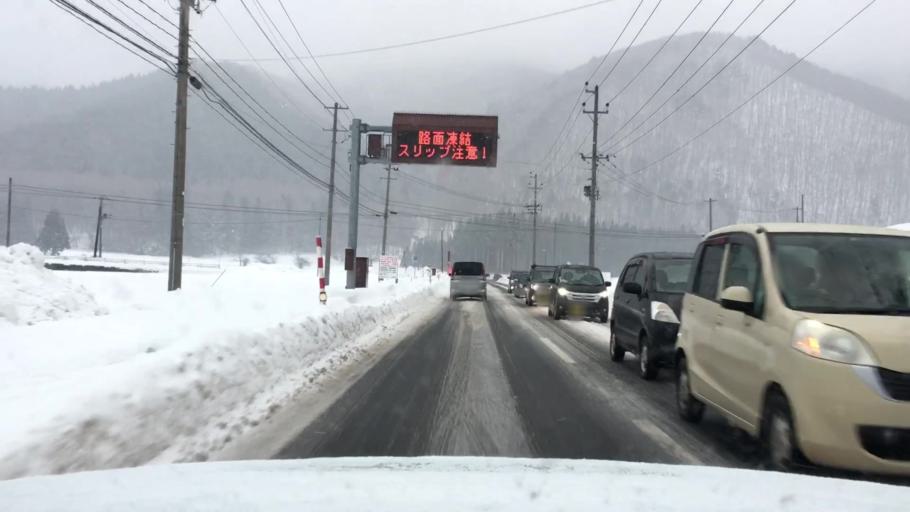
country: JP
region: Akita
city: Hanawa
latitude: 40.0786
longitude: 141.0224
